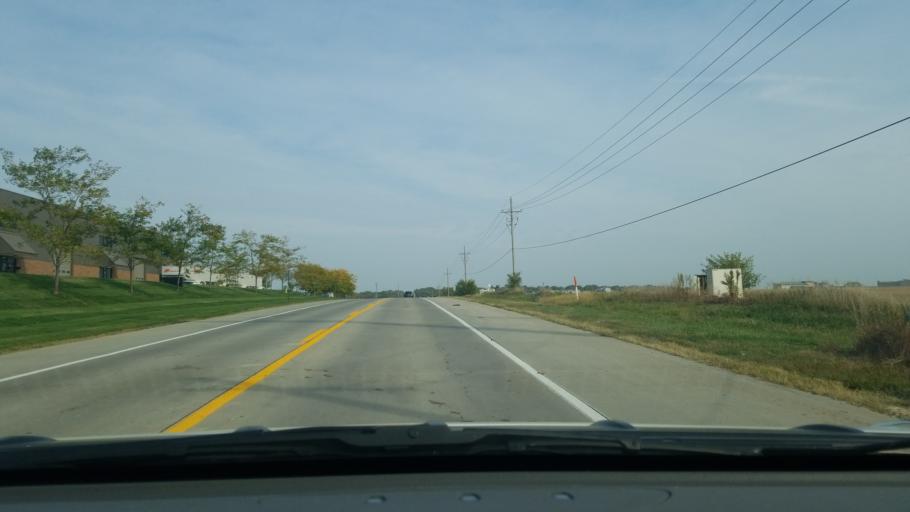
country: US
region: Nebraska
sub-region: Sarpy County
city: Chalco
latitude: 41.1690
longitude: -96.1196
